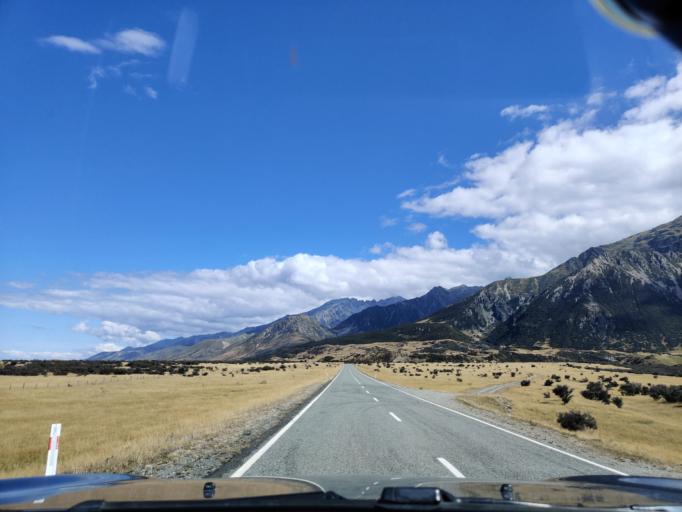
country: NZ
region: Canterbury
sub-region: Timaru District
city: Pleasant Point
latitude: -43.7937
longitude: 170.1174
